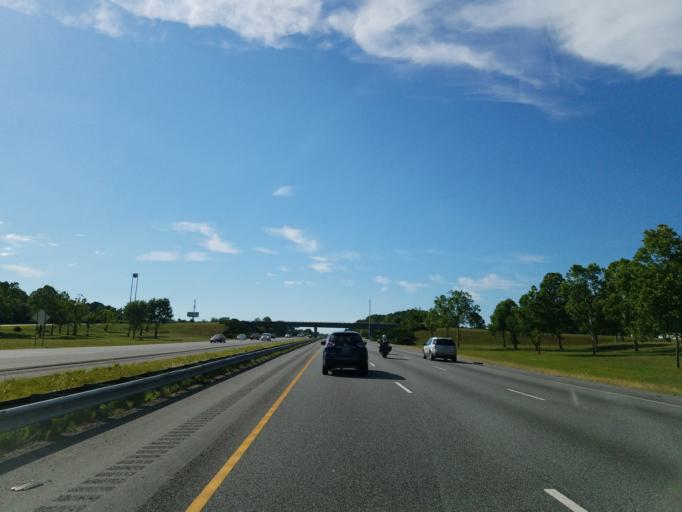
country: US
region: Georgia
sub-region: Bartow County
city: Cartersville
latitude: 34.2712
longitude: -84.8095
